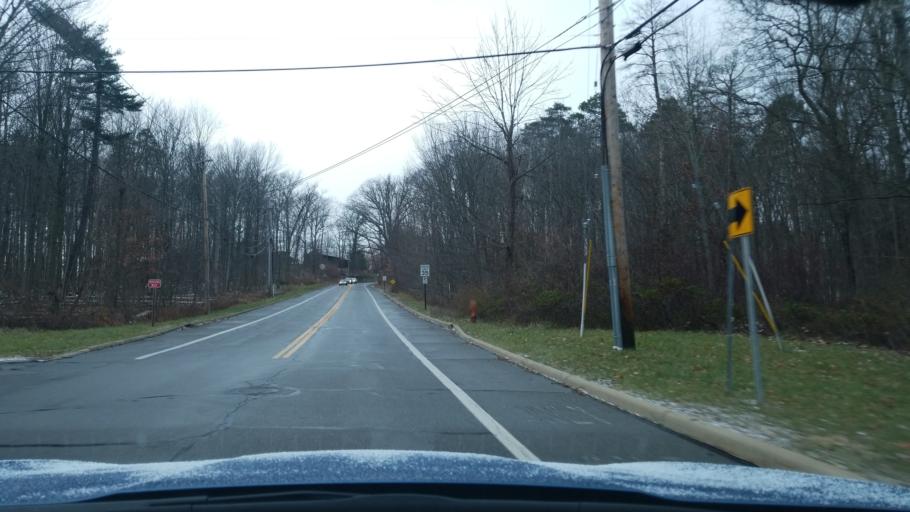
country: US
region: Ohio
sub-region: Cuyahoga County
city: North Olmsted
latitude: 41.4064
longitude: -81.8925
